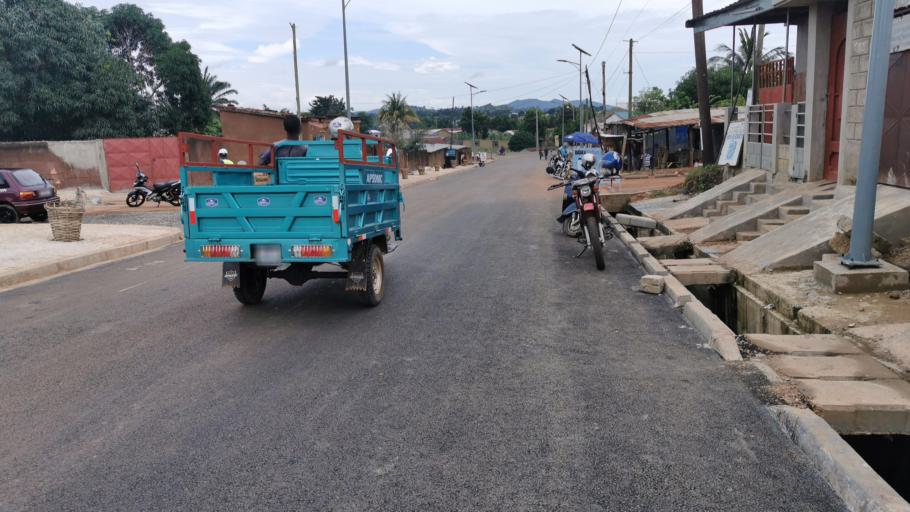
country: TG
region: Kara
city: Kara
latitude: 9.5548
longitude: 1.1939
